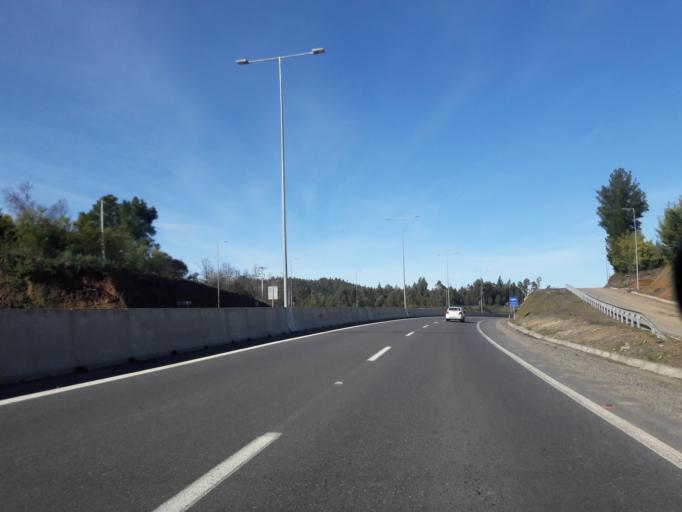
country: CL
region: Biobio
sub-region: Provincia de Biobio
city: Yumbel
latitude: -36.9324
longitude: -72.7634
